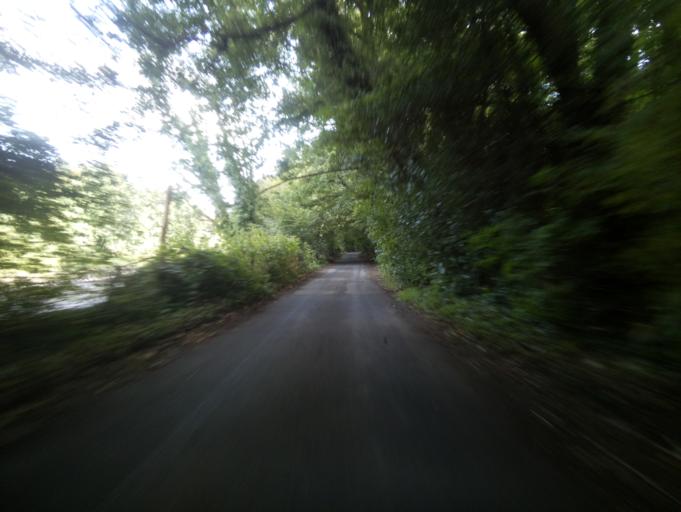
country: GB
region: Wales
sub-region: Caerphilly County Borough
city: Abertridwr
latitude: 51.5656
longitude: -3.2864
